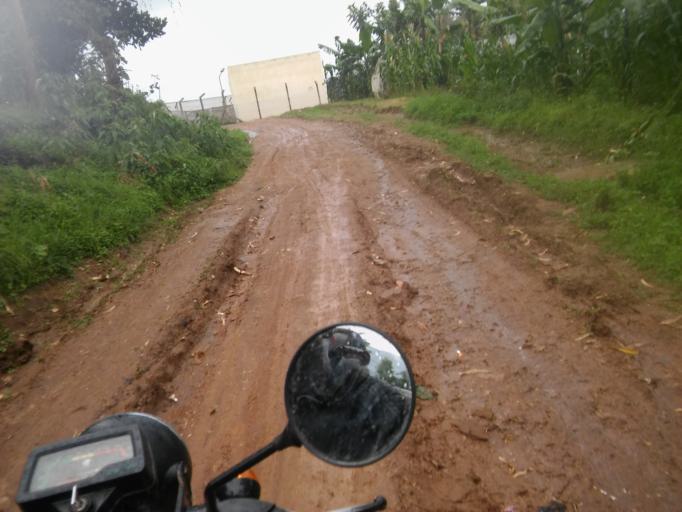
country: UG
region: Eastern Region
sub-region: Bududa District
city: Bududa
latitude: 0.9983
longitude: 34.2441
